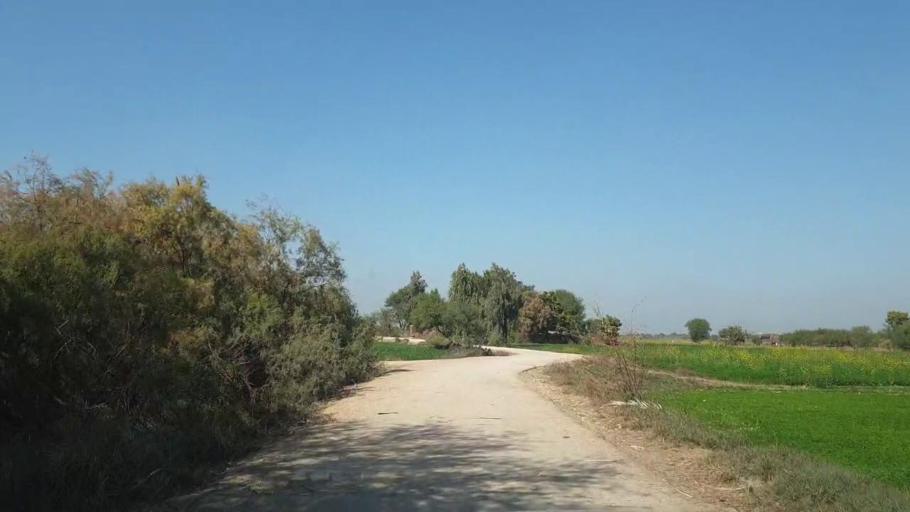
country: PK
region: Sindh
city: Tando Adam
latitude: 25.6512
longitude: 68.6997
